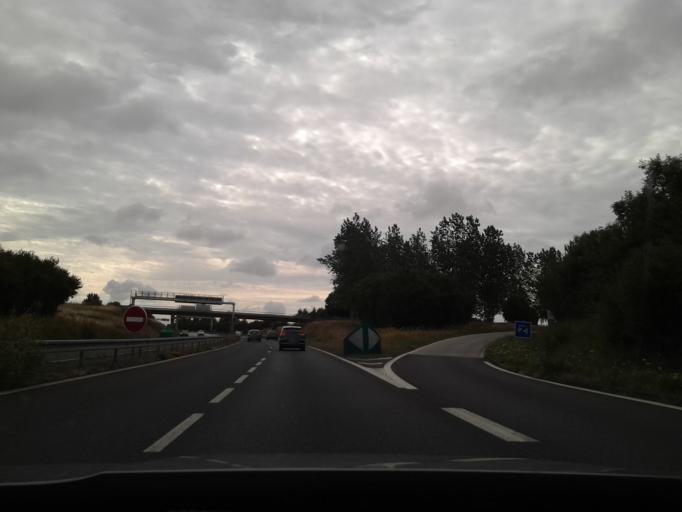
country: FR
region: Lower Normandy
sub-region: Departement de la Manche
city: Saint-Hilaire-Petitville
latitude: 49.3057
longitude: -1.2126
